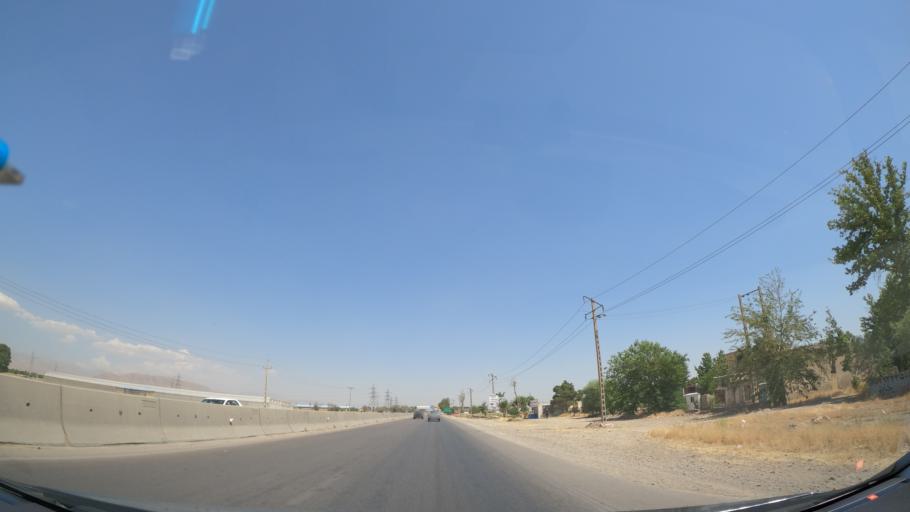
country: IR
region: Alborz
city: Hashtgerd
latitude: 35.9259
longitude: 50.7370
